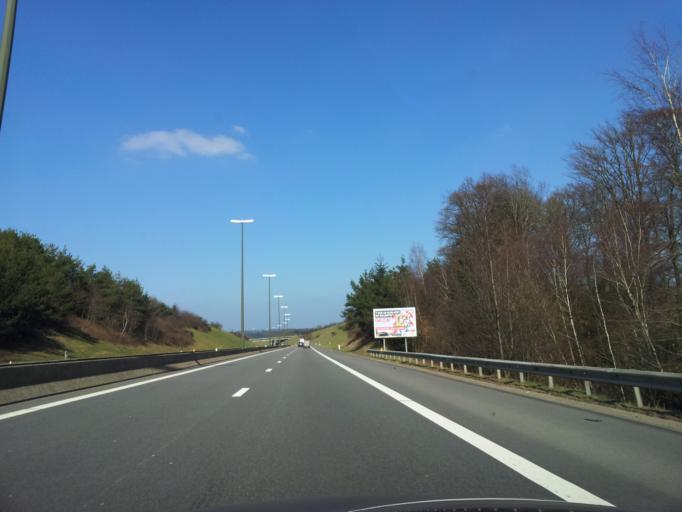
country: BE
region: Wallonia
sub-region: Province de Liege
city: Jalhay
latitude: 50.5088
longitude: 5.9476
